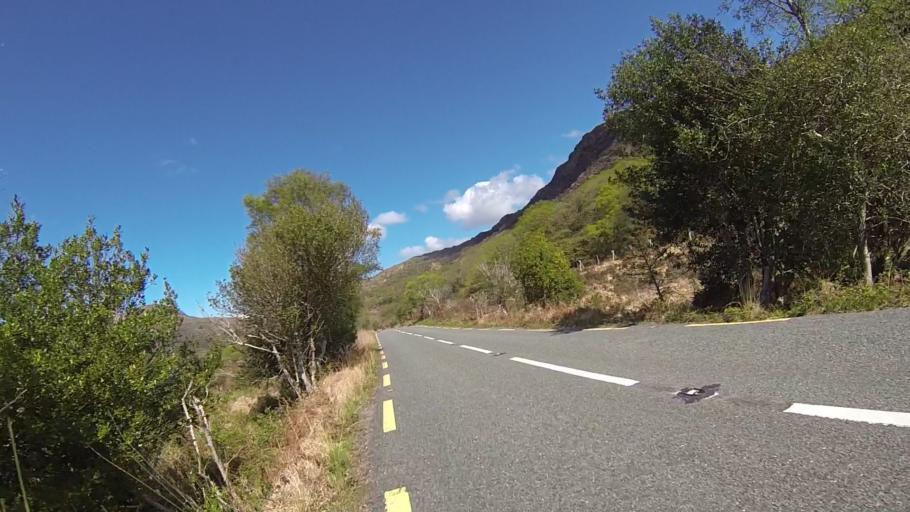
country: IE
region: Munster
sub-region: Ciarrai
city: Kenmare
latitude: 51.9740
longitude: -9.5797
